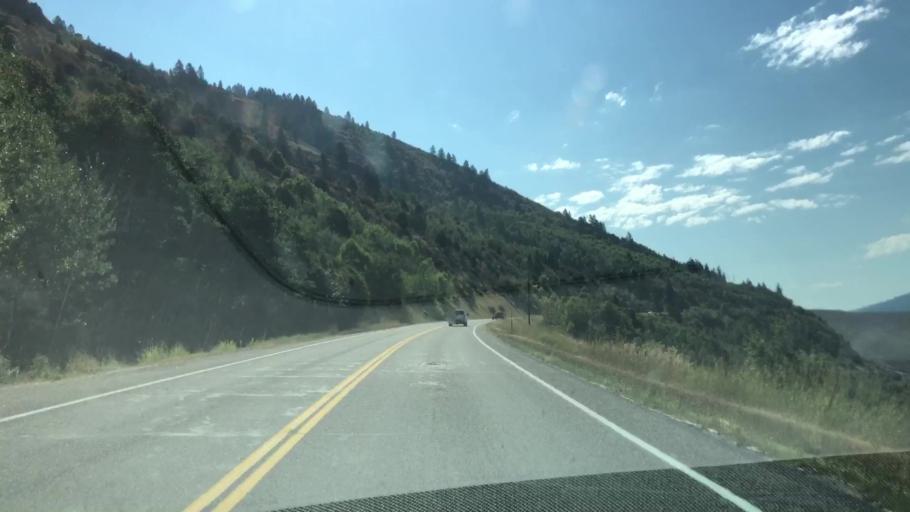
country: US
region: Idaho
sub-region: Teton County
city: Victor
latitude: 43.3431
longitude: -111.2038
